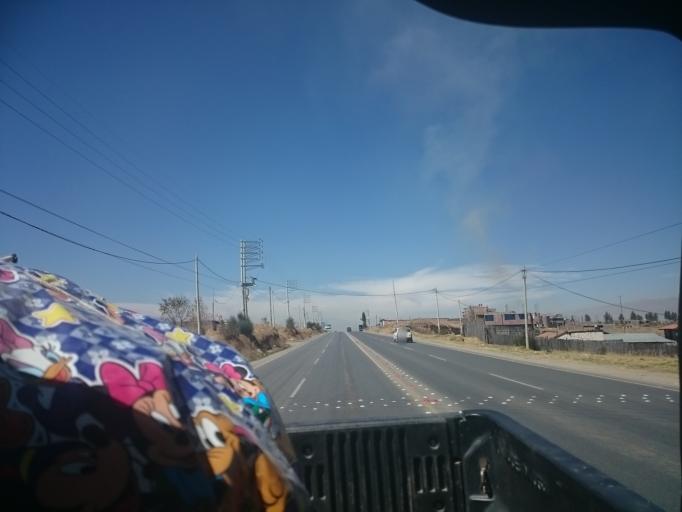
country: PE
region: Junin
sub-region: Provincia de Huancayo
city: San Agustin
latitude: -11.9827
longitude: -75.2622
